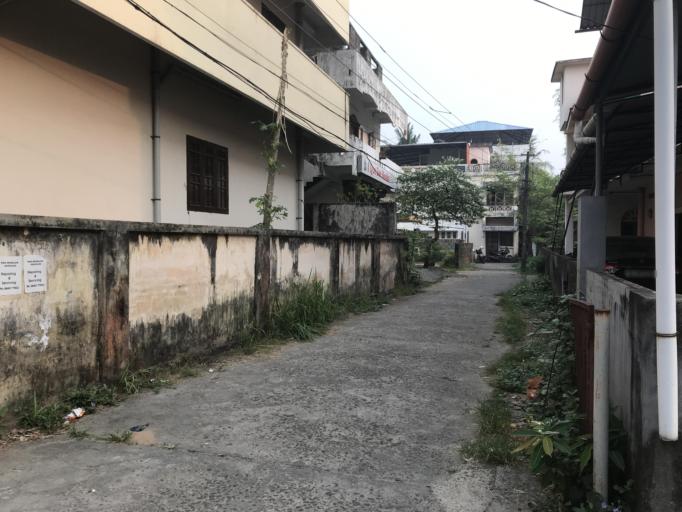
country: IN
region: Kerala
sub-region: Ernakulam
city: Elur
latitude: 10.0043
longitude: 76.2923
